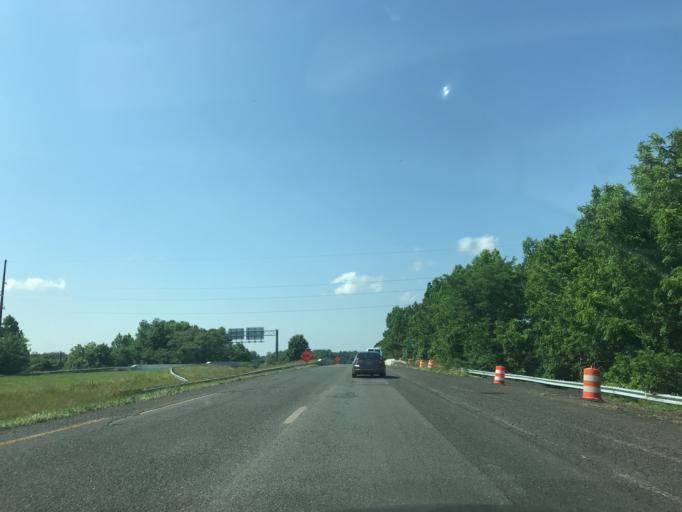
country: US
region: Maryland
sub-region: Wicomico County
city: Salisbury
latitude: 38.3791
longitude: -75.5396
